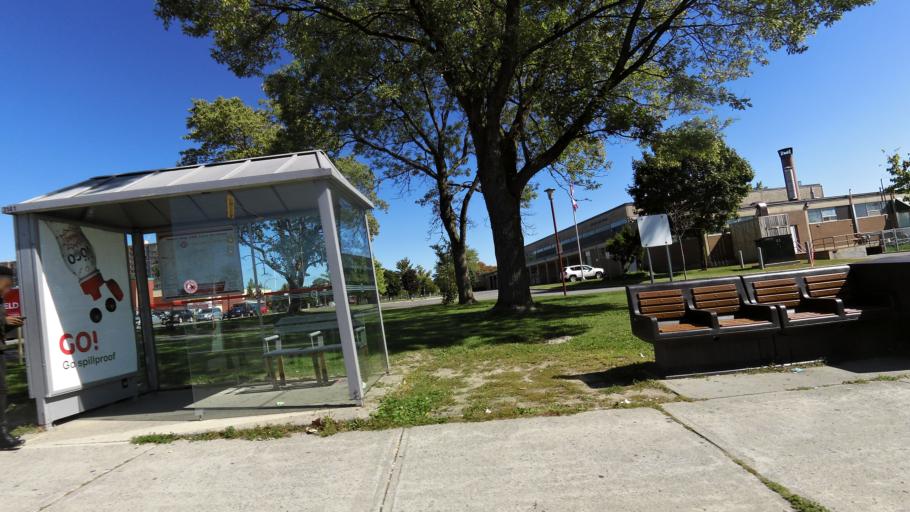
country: CA
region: Ontario
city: Ottawa
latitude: 45.3436
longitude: -75.7291
